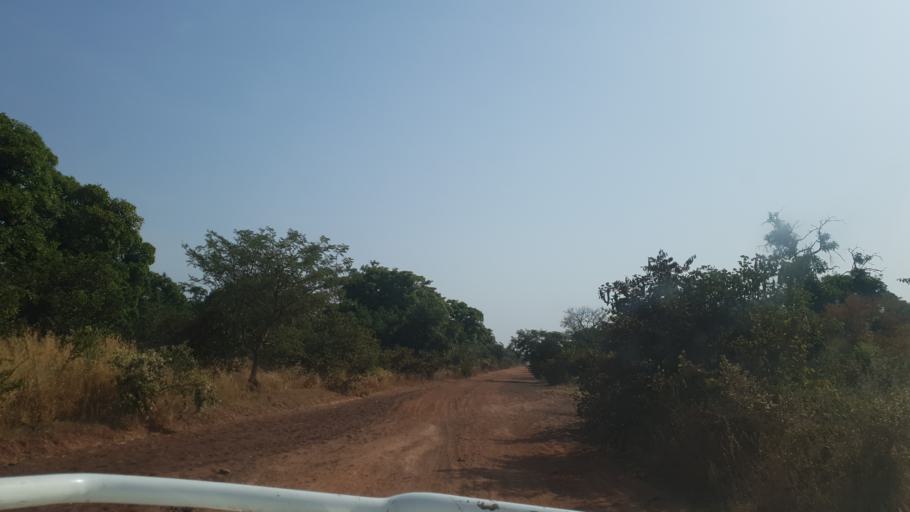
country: ML
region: Koulikoro
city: Dioila
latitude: 12.6684
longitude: -6.6830
